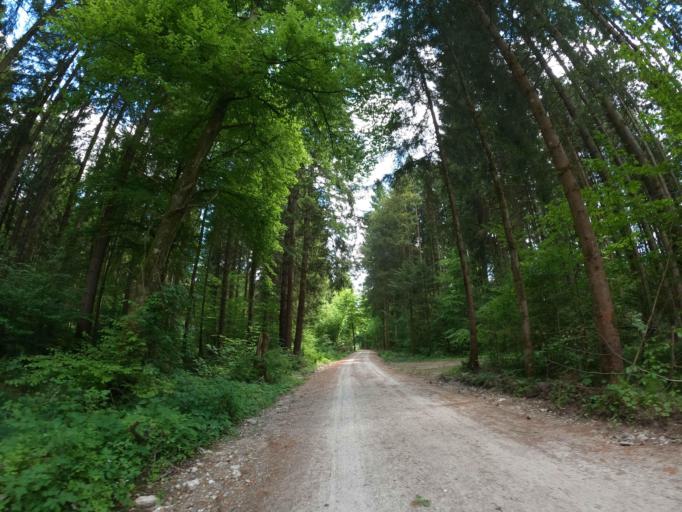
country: DE
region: Bavaria
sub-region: Upper Bavaria
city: Aying
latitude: 47.9603
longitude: 11.7498
